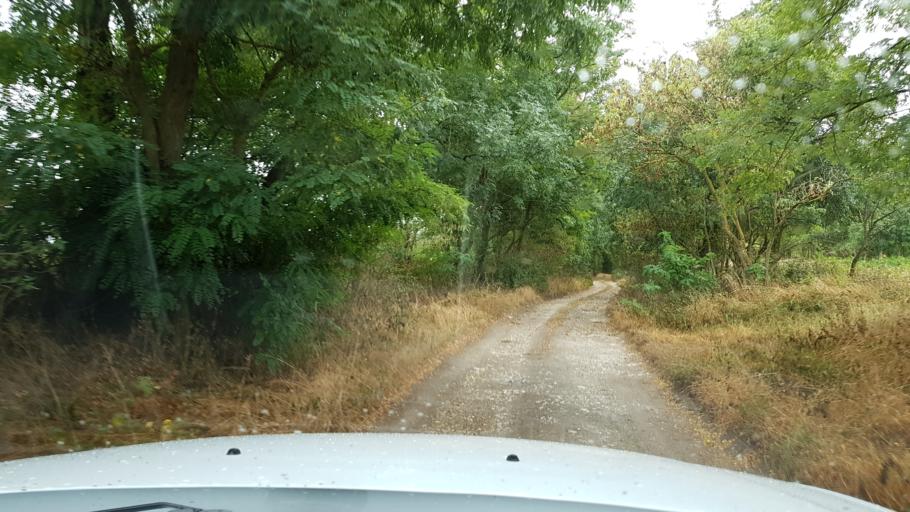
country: PL
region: West Pomeranian Voivodeship
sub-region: Powiat gryfinski
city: Cedynia
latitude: 52.8471
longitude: 14.2875
